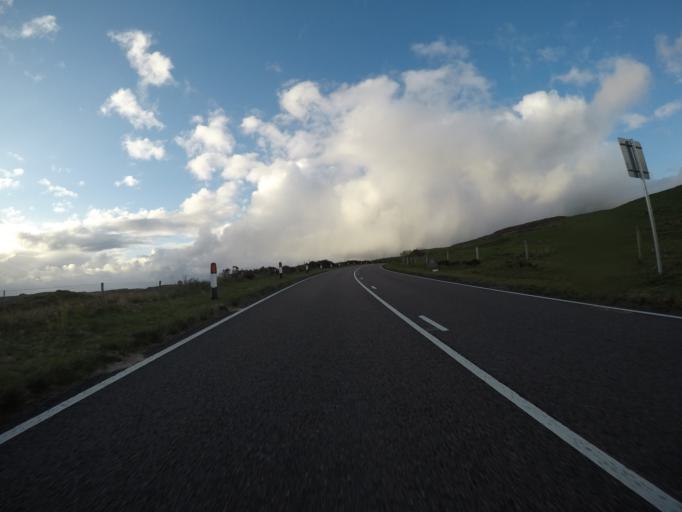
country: GB
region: Scotland
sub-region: Highland
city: Portree
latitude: 57.5454
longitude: -6.3654
